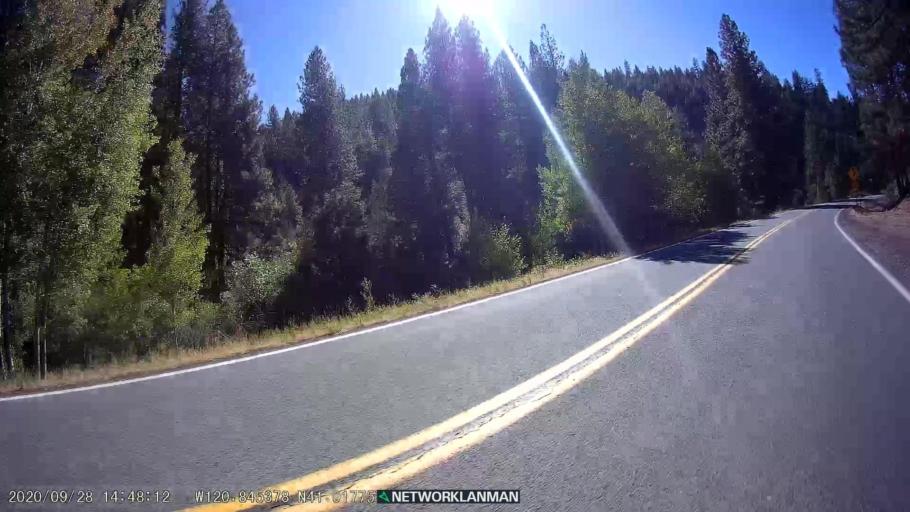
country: US
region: California
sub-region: Modoc County
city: Alturas
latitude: 41.0175
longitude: -120.8457
